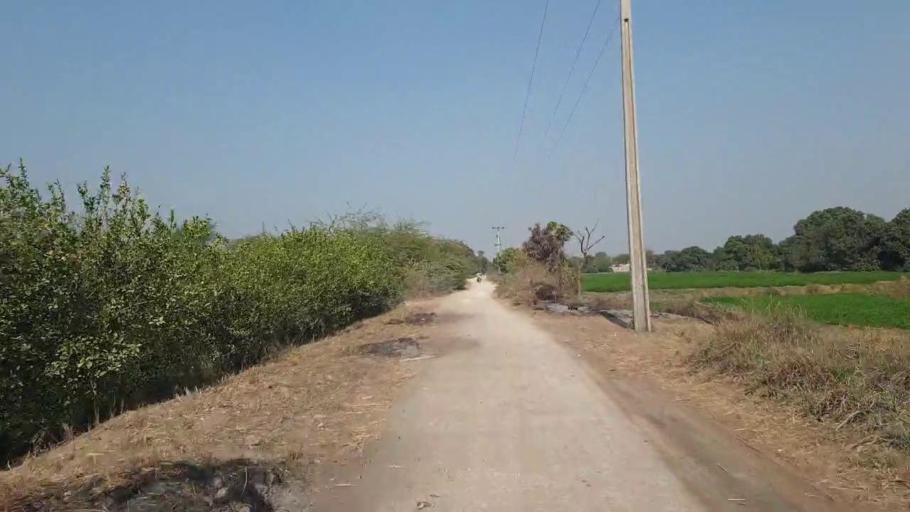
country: PK
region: Sindh
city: Chambar
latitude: 25.4075
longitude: 68.8958
